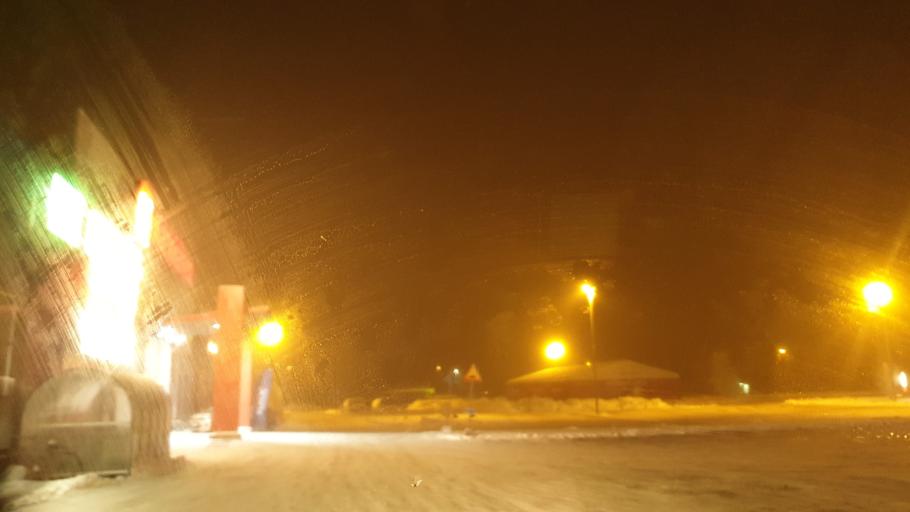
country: FI
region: Northern Ostrobothnia
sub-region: Oulunkaari
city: Ii
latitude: 65.2905
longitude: 25.3748
